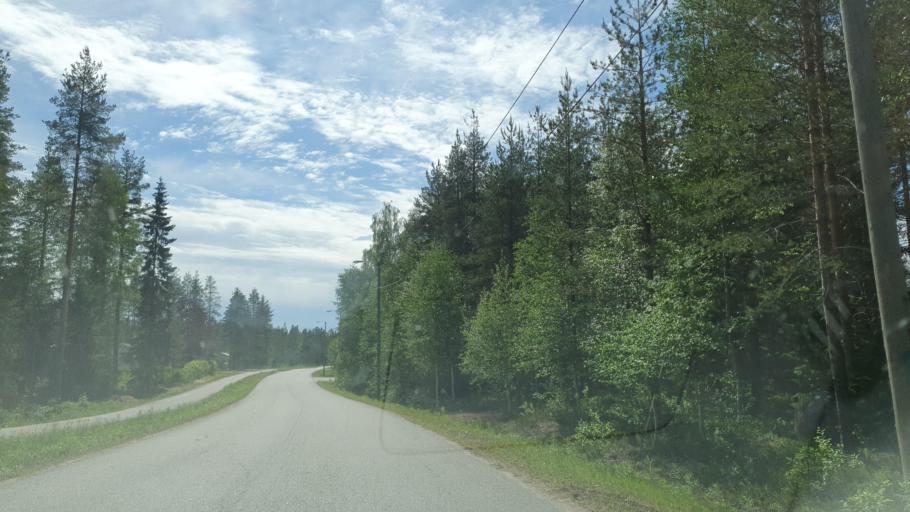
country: FI
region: Kainuu
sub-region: Kehys-Kainuu
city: Hyrynsalmi
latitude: 64.6896
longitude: 28.4696
